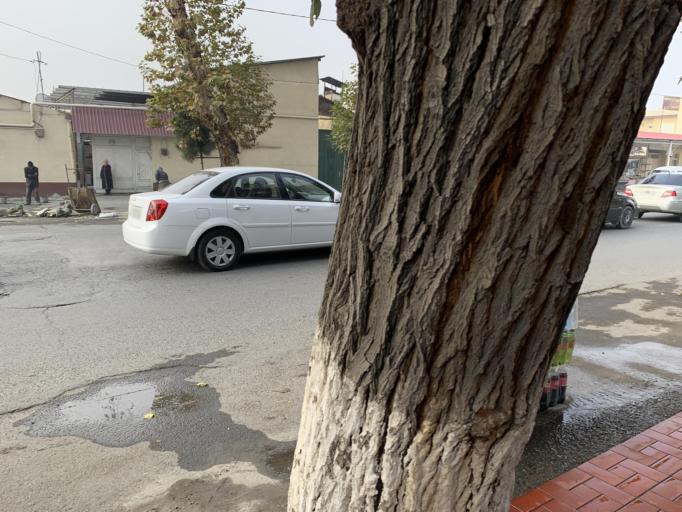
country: UZ
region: Fergana
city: Qo`qon
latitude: 40.5433
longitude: 70.9516
